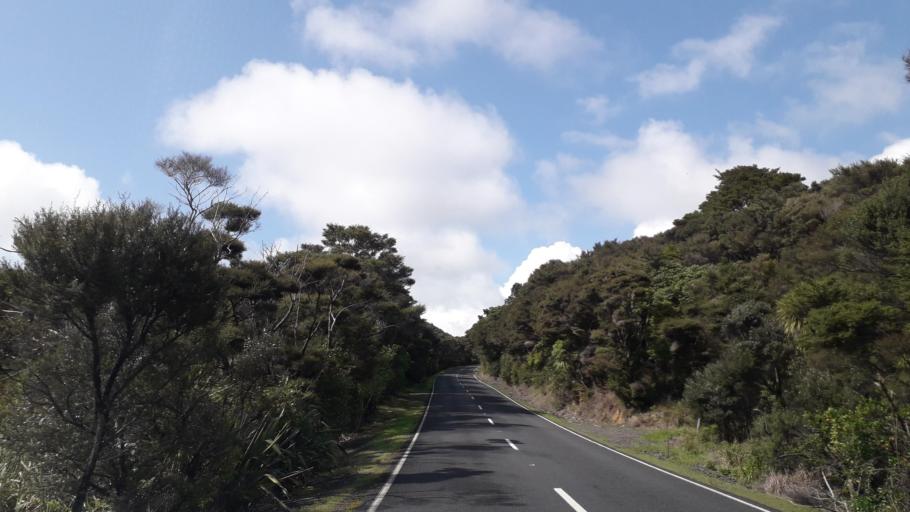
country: NZ
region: Northland
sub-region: Far North District
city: Paihia
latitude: -35.2481
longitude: 174.2581
